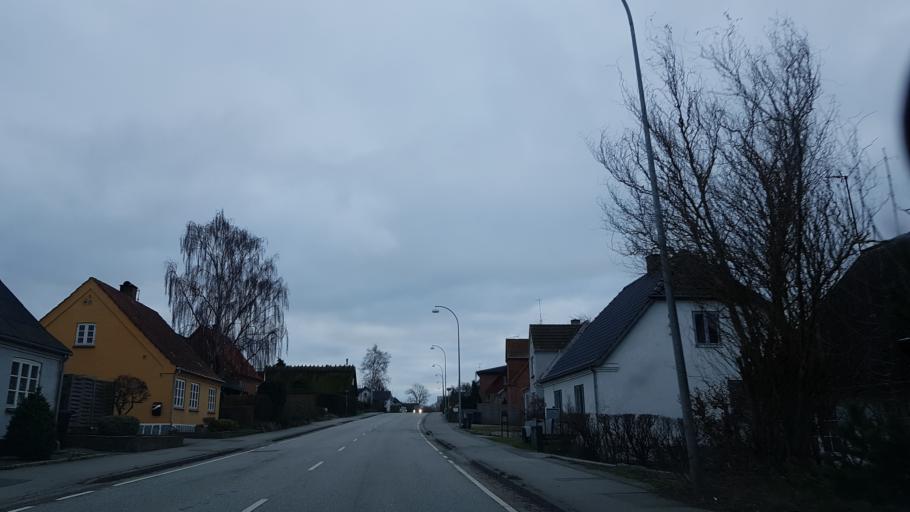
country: DK
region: Zealand
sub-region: Holbaek Kommune
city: Jyderup
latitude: 55.7153
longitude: 11.3833
